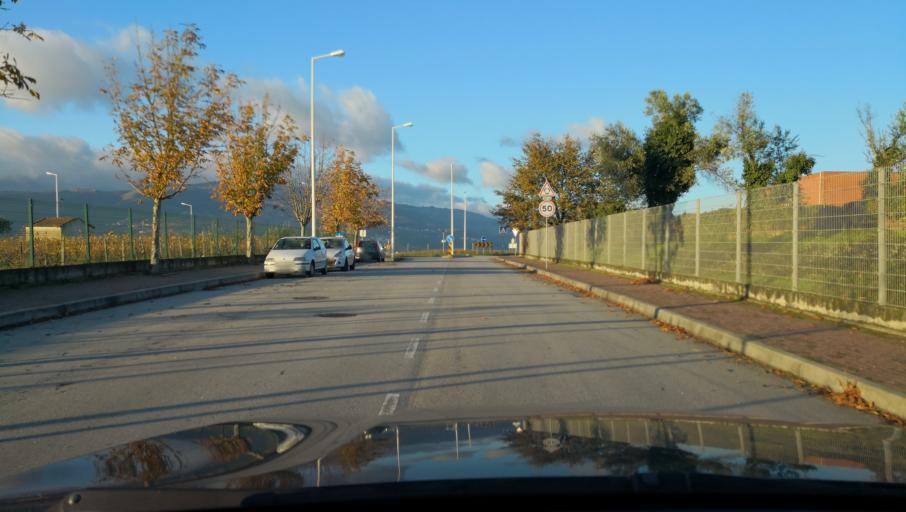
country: PT
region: Vila Real
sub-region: Vila Real
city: Vila Real
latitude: 41.2837
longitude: -7.7380
